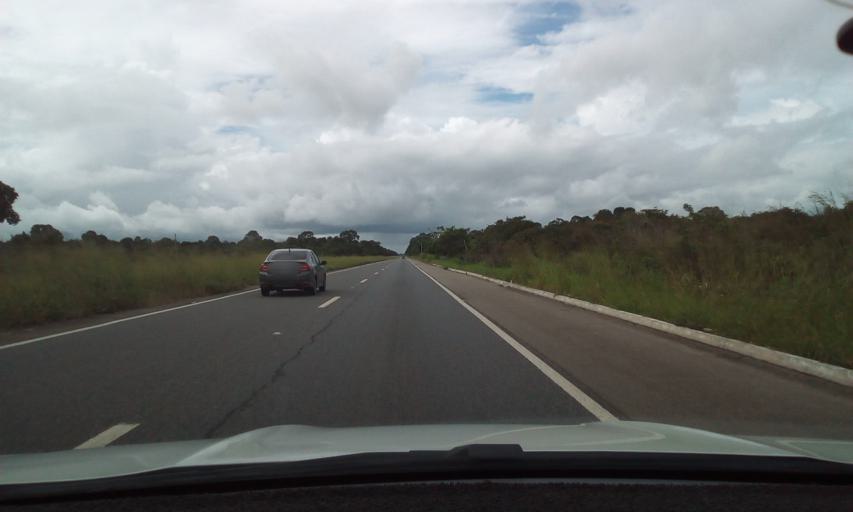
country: BR
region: Paraiba
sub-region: Cruz Do Espirito Santo
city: Cruz do Espirito Santo
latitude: -7.2028
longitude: -35.1101
